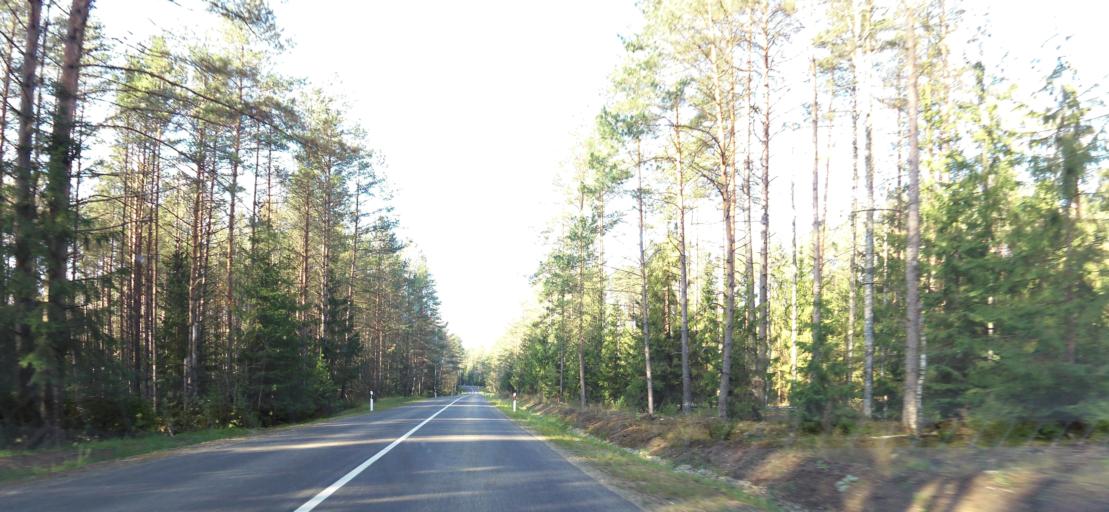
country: LT
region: Vilnius County
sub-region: Trakai
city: Rudiskes
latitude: 54.5099
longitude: 24.9030
